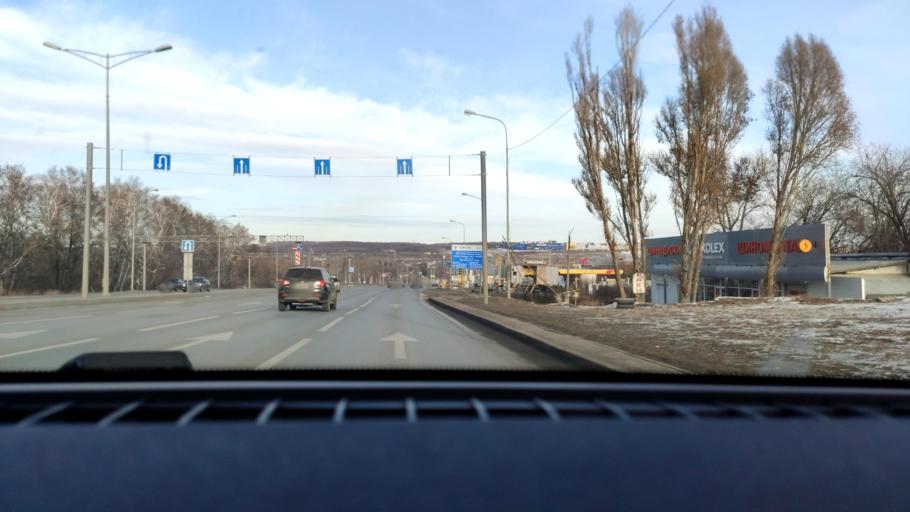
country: RU
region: Samara
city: Petra-Dubrava
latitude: 53.3106
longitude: 50.2916
